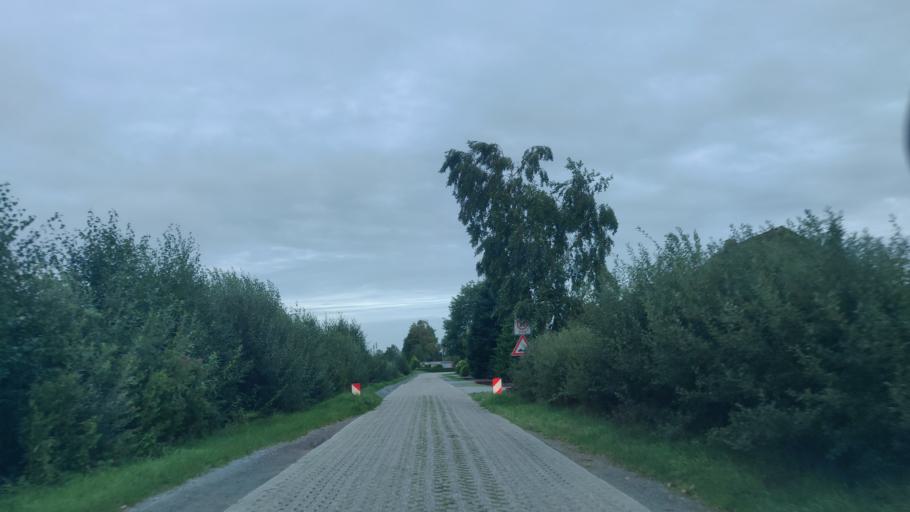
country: DE
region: Lower Saxony
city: Aurich
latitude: 53.4832
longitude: 7.4059
